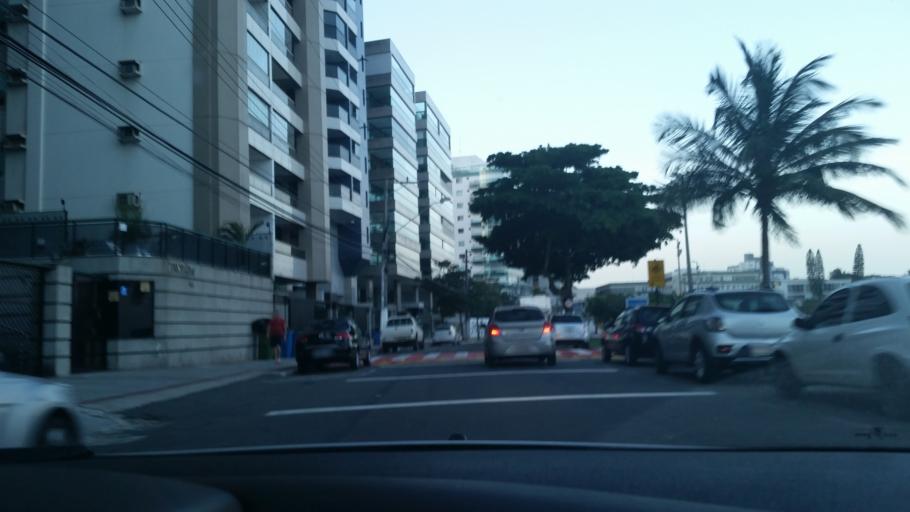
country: BR
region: Espirito Santo
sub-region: Vila Velha
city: Vila Velha
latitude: -20.3311
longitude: -40.2740
